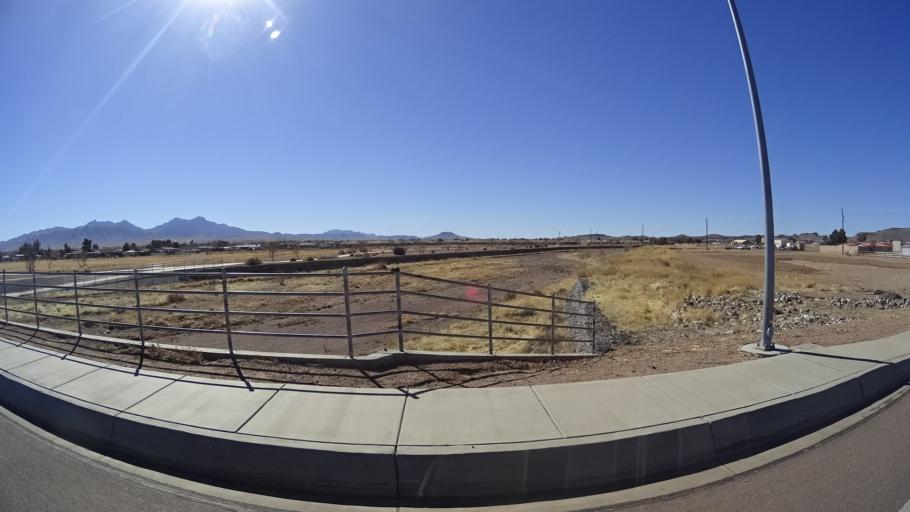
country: US
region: Arizona
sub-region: Mohave County
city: New Kingman-Butler
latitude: 35.2395
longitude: -114.0222
